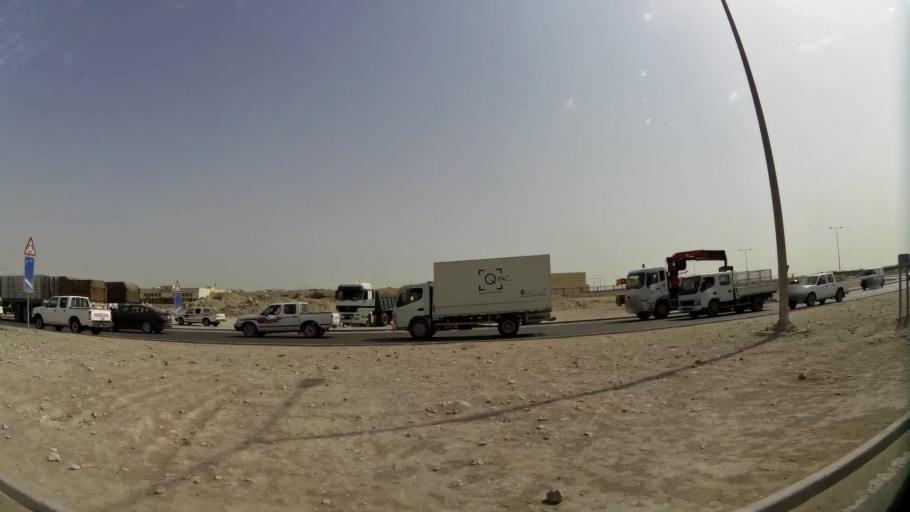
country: QA
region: Al Wakrah
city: Al Wukayr
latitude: 25.1834
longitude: 51.4616
